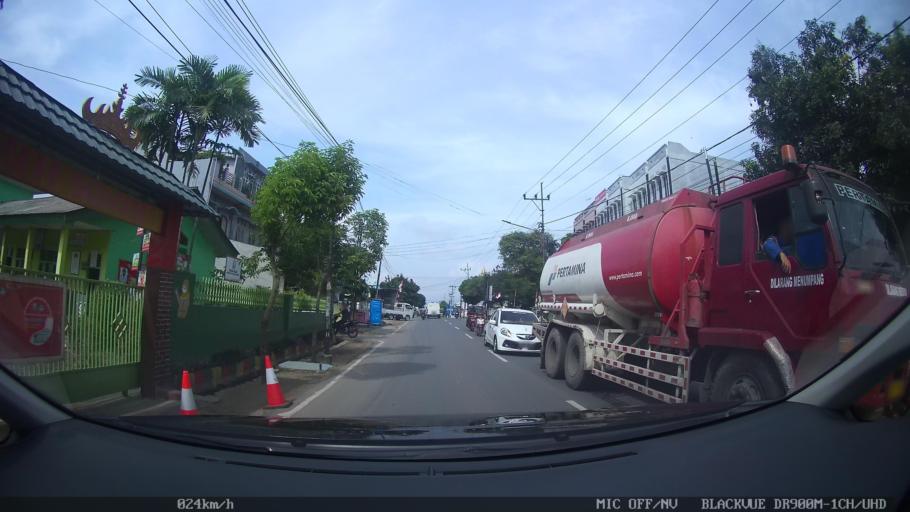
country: ID
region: Lampung
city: Kedaton
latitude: -5.3855
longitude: 105.2938
